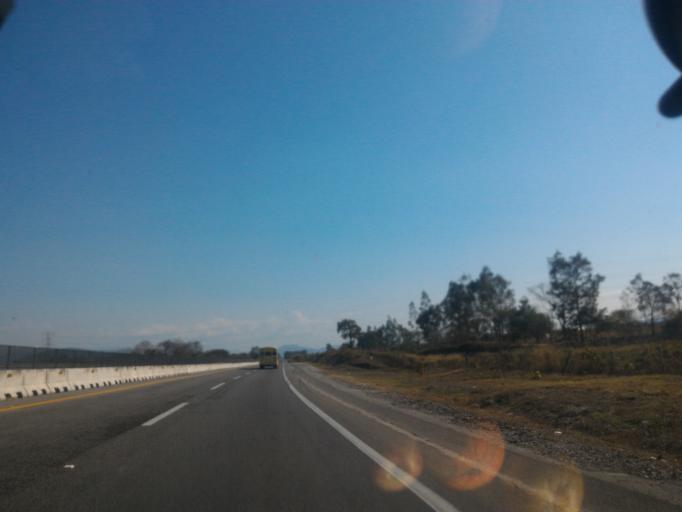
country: MX
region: Jalisco
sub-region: Zapotlan el Grande
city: Ciudad Guzman [CERESO]
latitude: 19.6407
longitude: -103.4695
